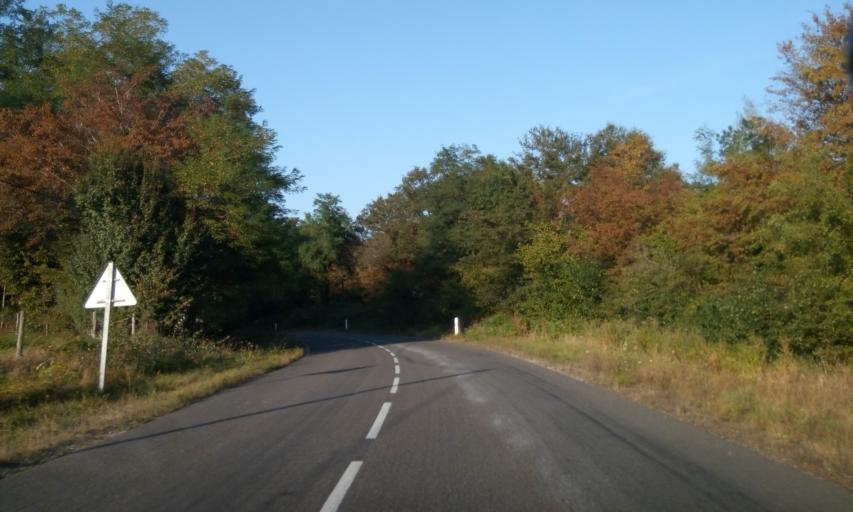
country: FR
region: Rhone-Alpes
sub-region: Departement de l'Ain
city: Chalamont
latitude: 46.0134
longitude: 5.2038
